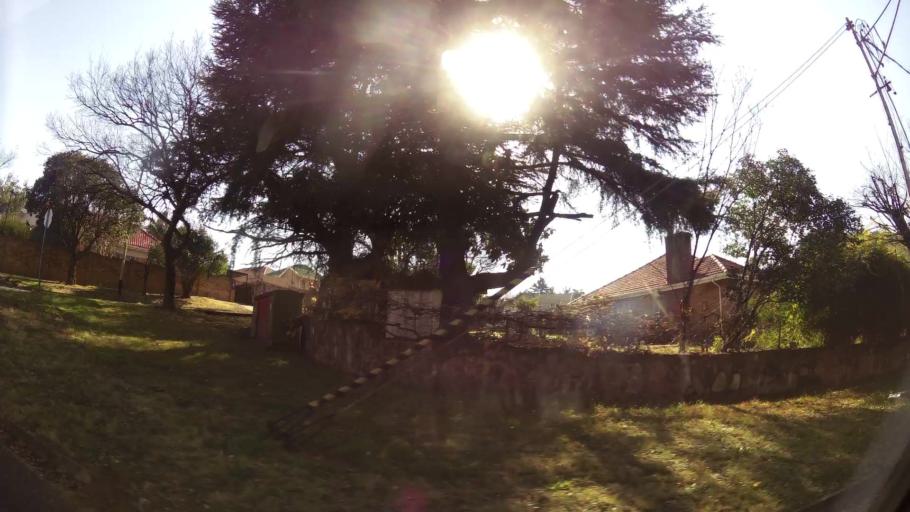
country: ZA
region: Gauteng
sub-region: City of Johannesburg Metropolitan Municipality
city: Johannesburg
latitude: -26.2612
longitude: 28.0697
